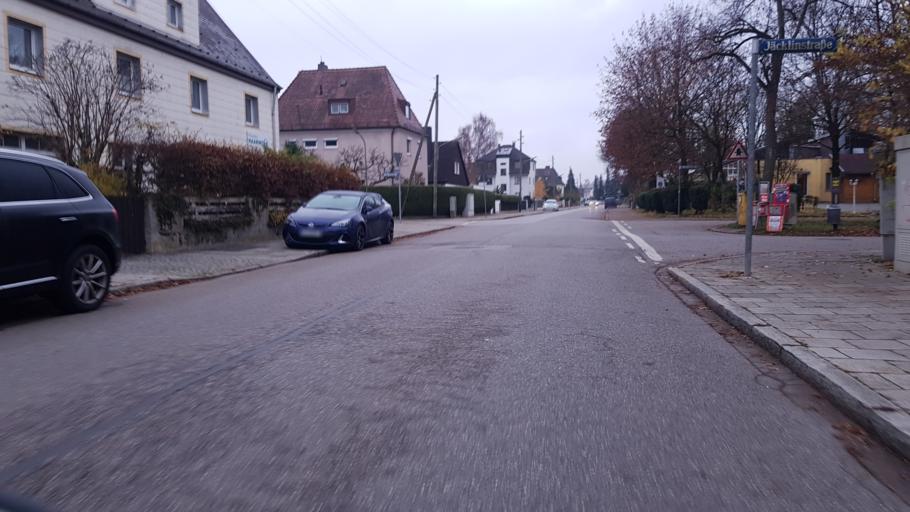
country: DE
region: Bavaria
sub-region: Upper Bavaria
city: Bogenhausen
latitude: 48.1159
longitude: 11.6255
